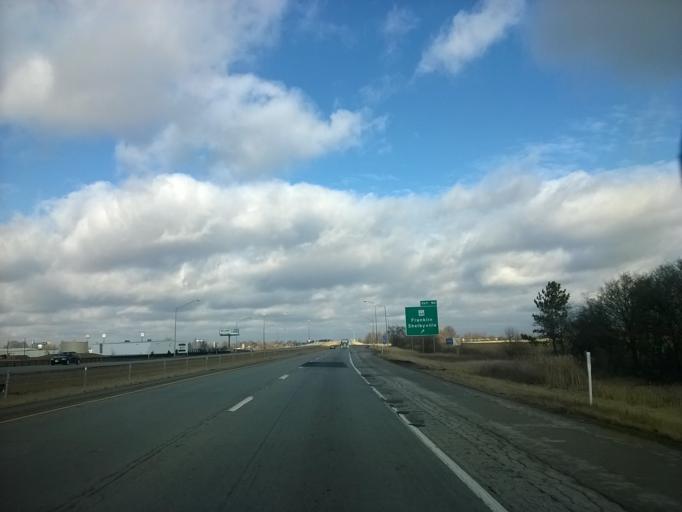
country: US
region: Indiana
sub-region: Johnson County
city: Franklin
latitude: 39.4764
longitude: -86.0118
